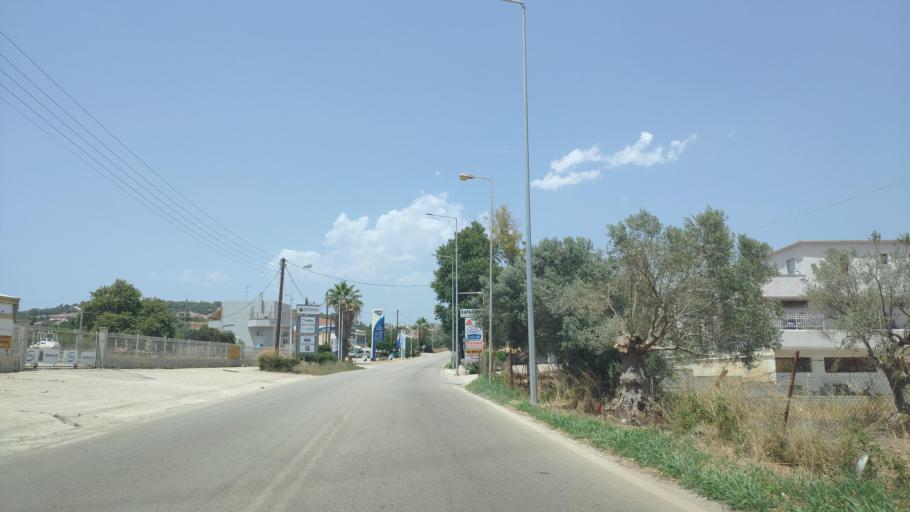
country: GR
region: Peloponnese
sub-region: Nomos Argolidos
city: Kranidi
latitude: 37.3648
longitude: 23.1625
